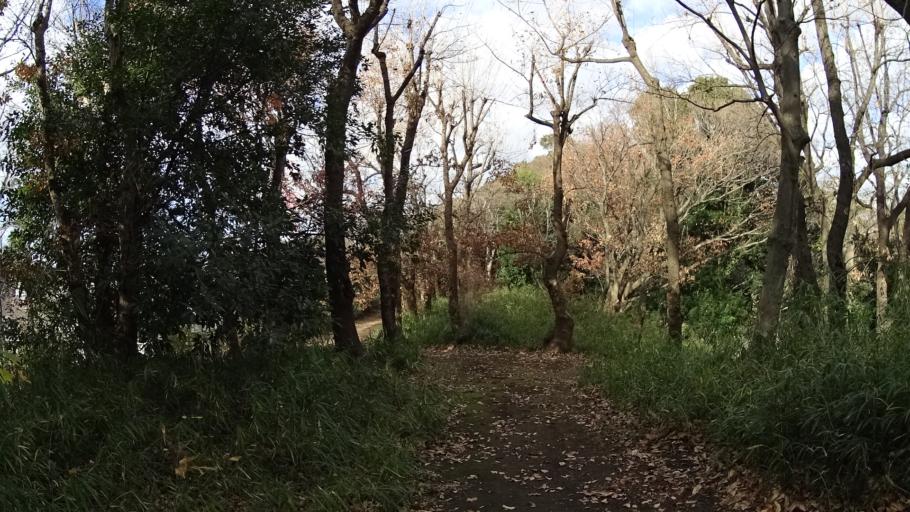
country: JP
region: Kanagawa
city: Yokohama
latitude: 35.4131
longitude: 139.5541
